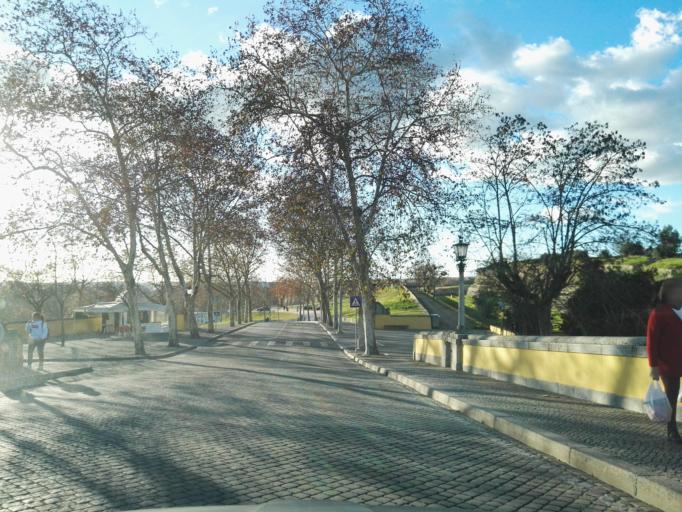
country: PT
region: Portalegre
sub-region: Elvas
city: Elvas
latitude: 38.8783
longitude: -7.1668
